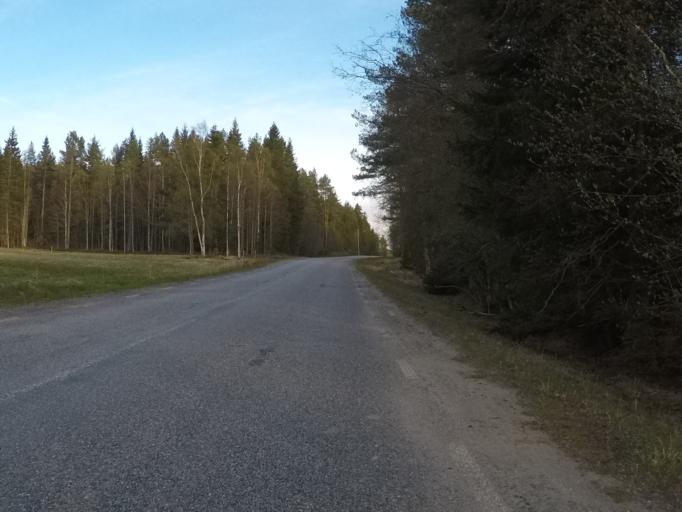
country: SE
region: Vaesterbotten
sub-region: Robertsfors Kommun
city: Robertsfors
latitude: 63.9919
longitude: 20.8100
